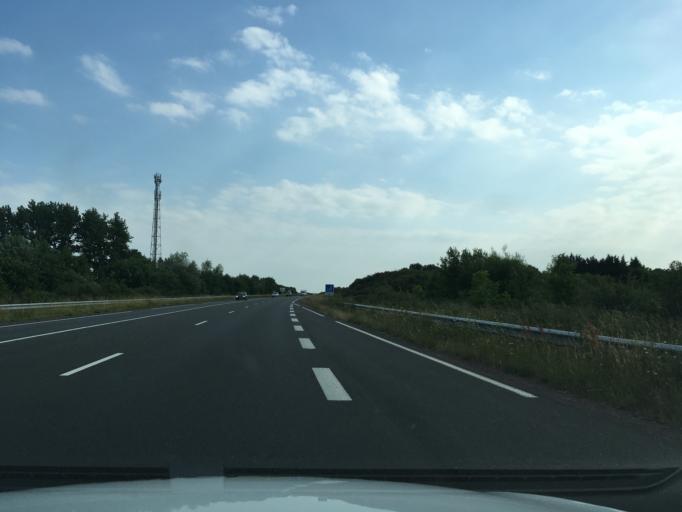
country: FR
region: Poitou-Charentes
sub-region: Departement des Deux-Sevres
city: Saint-Pardoux
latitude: 46.5429
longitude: -0.3130
